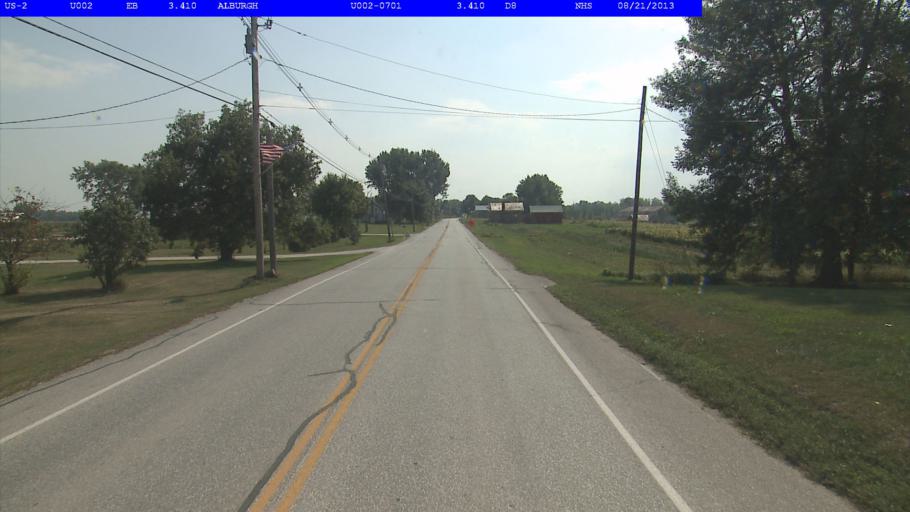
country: US
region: New York
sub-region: Clinton County
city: Rouses Point
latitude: 44.9847
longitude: -73.2969
